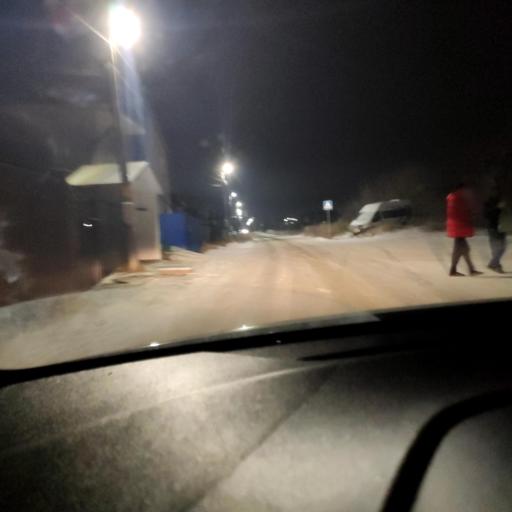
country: RU
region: Tatarstan
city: Staroye Arakchino
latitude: 55.8851
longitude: 49.0394
